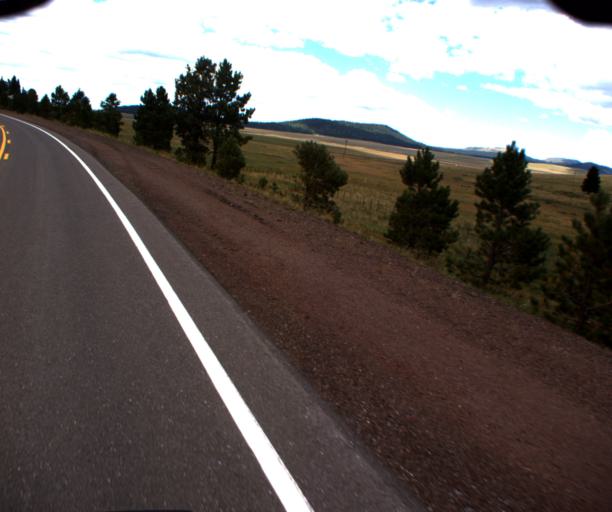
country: US
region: Arizona
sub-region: Apache County
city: Eagar
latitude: 34.0020
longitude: -109.5299
